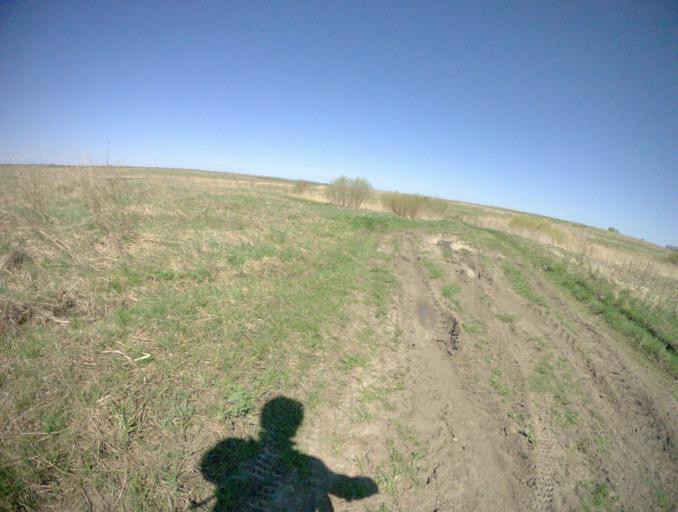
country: RU
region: Vladimir
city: Vladimir
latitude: 56.2866
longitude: 40.3484
